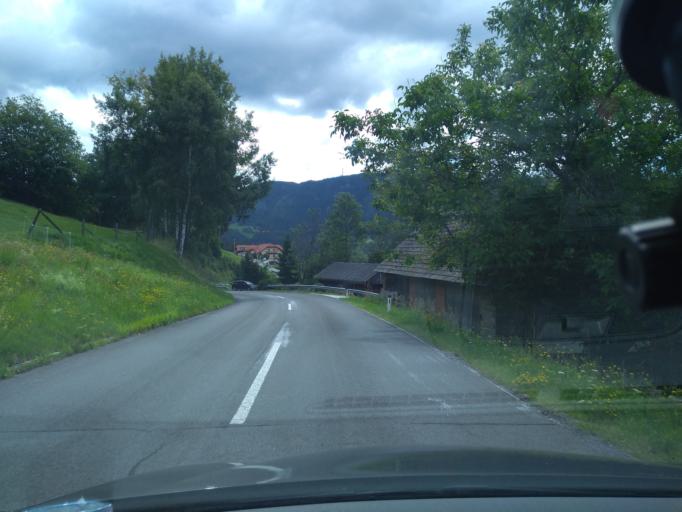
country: AT
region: Styria
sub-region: Politischer Bezirk Graz-Umgebung
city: Semriach
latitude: 47.2212
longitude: 15.4248
